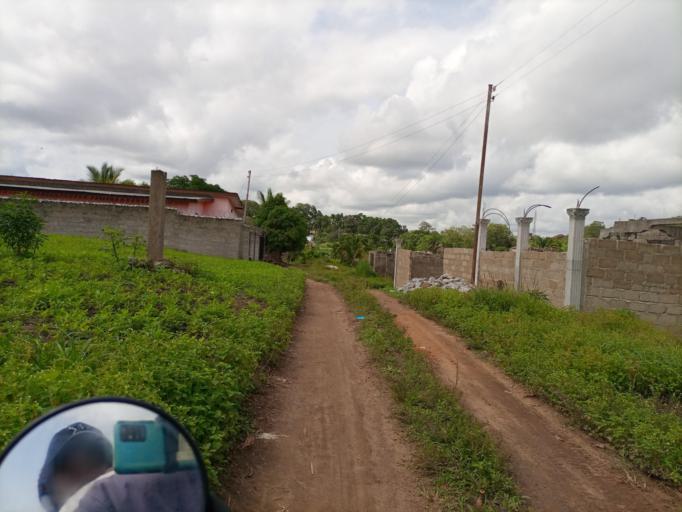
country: SL
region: Southern Province
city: Bo
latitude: 7.9723
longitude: -11.7569
